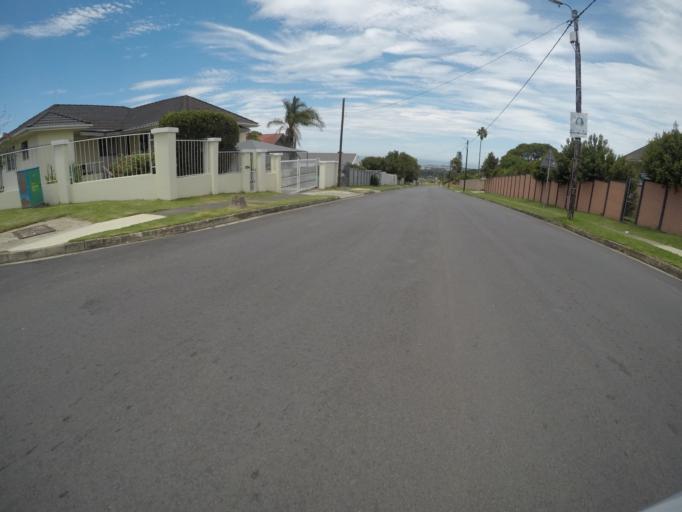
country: ZA
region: Eastern Cape
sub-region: Buffalo City Metropolitan Municipality
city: East London
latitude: -33.0371
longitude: 27.8554
